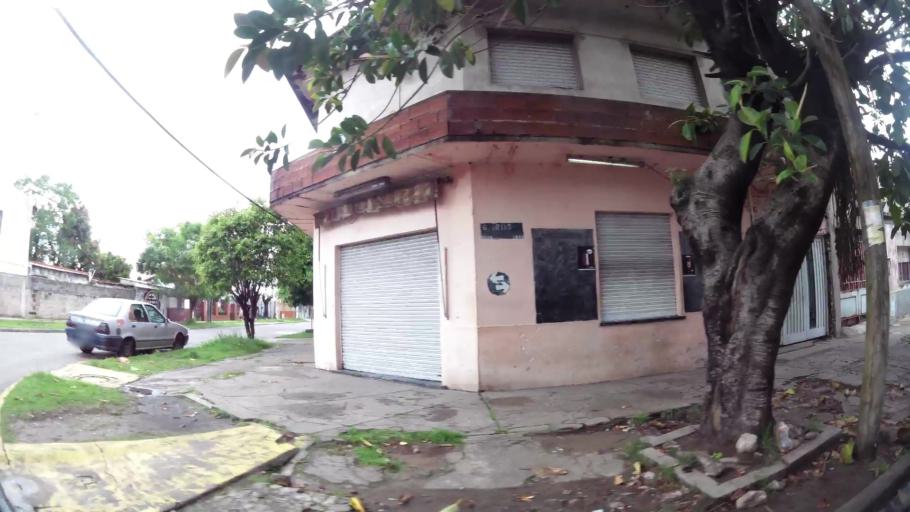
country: AR
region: Buenos Aires
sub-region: Partido de Lanus
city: Lanus
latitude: -34.7250
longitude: -58.3722
